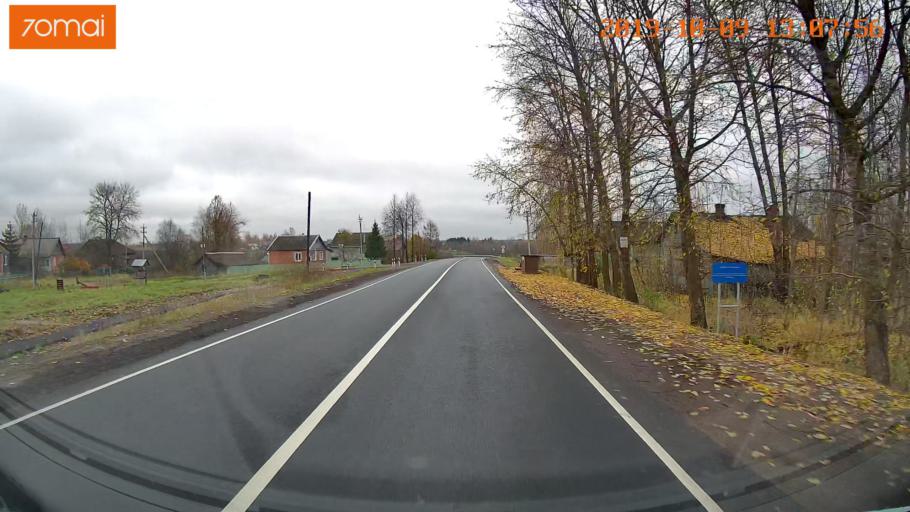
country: RU
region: Jaroslavl
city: Lyubim
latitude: 58.3563
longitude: 40.6554
